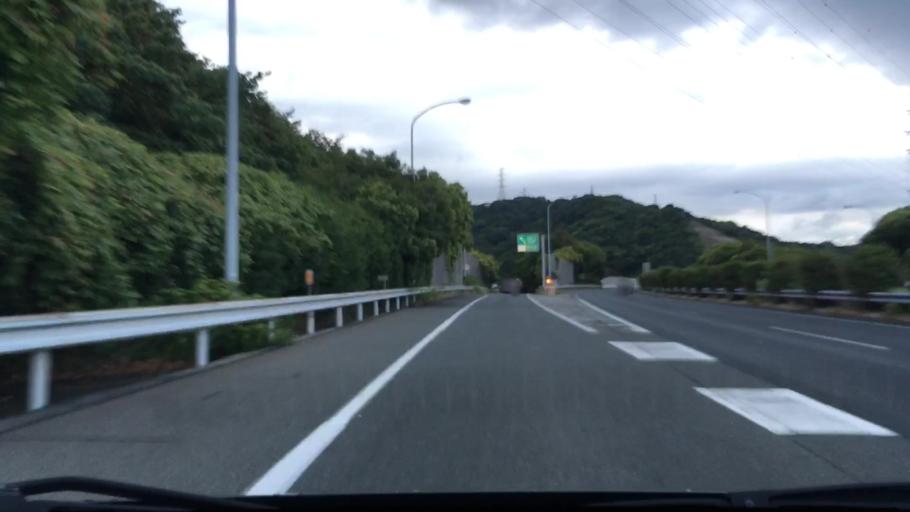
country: JP
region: Yamaguchi
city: Shimonoseki
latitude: 33.8849
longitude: 130.9696
